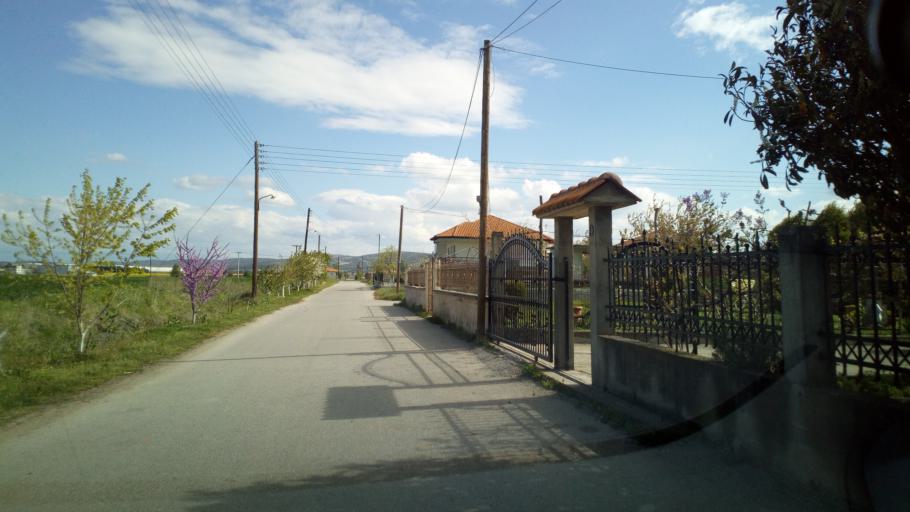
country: GR
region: Central Macedonia
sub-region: Nomos Kilkis
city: Gallikos
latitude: 40.8326
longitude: 22.8911
